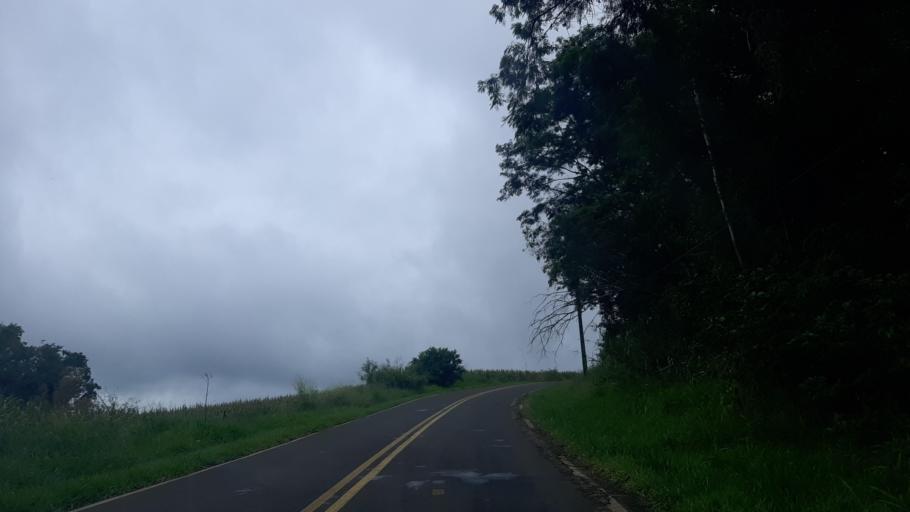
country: BR
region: Parana
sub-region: Ampere
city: Ampere
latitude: -25.9846
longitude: -53.4430
